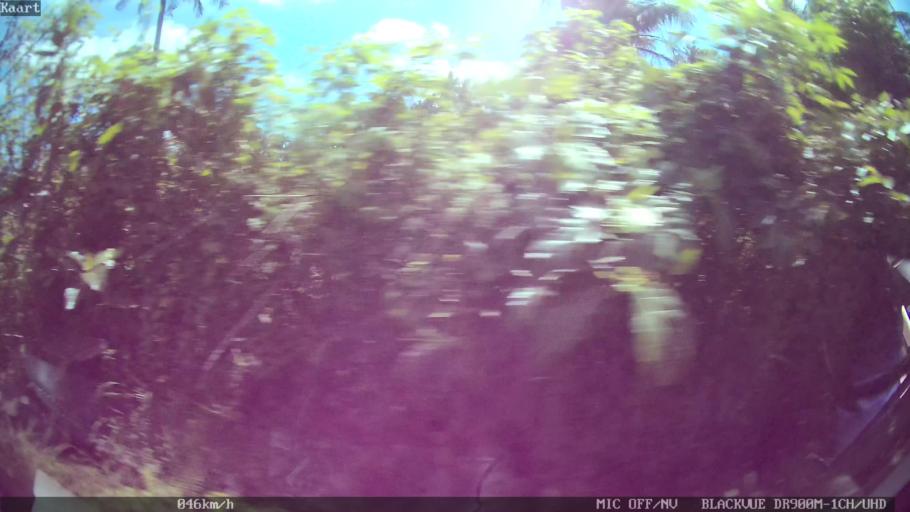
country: ID
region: Bali
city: Banjar Kelodan
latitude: -8.5202
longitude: 115.3336
